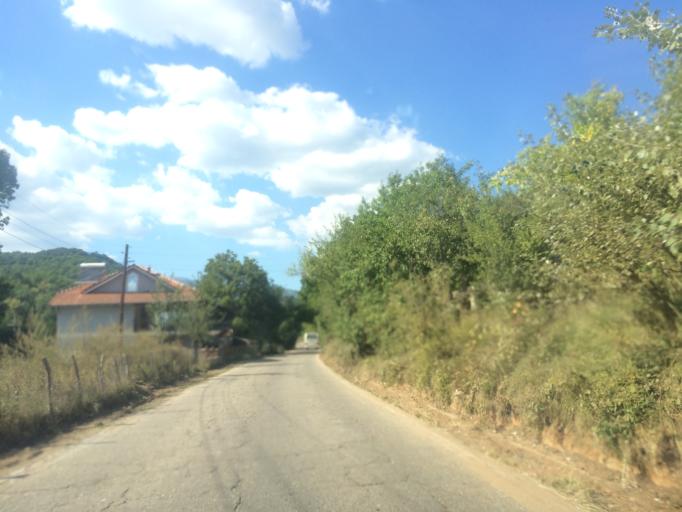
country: MK
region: Makedonska Kamenica
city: Makedonska Kamenica
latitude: 42.0429
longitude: 22.5751
